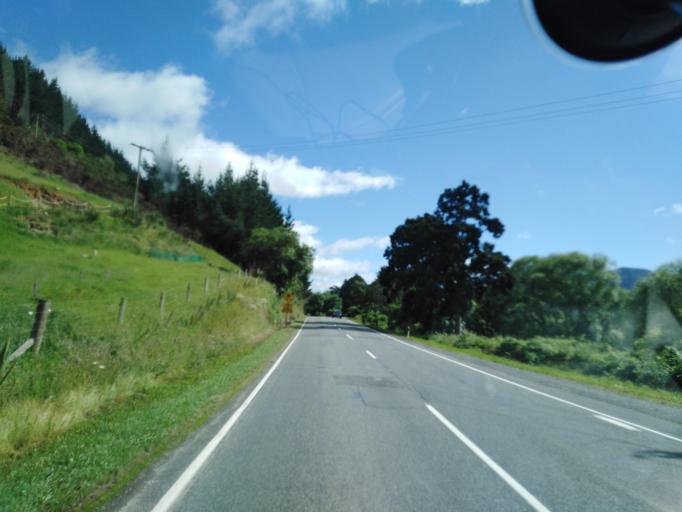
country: NZ
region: Nelson
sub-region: Nelson City
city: Nelson
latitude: -41.2595
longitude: 173.5752
